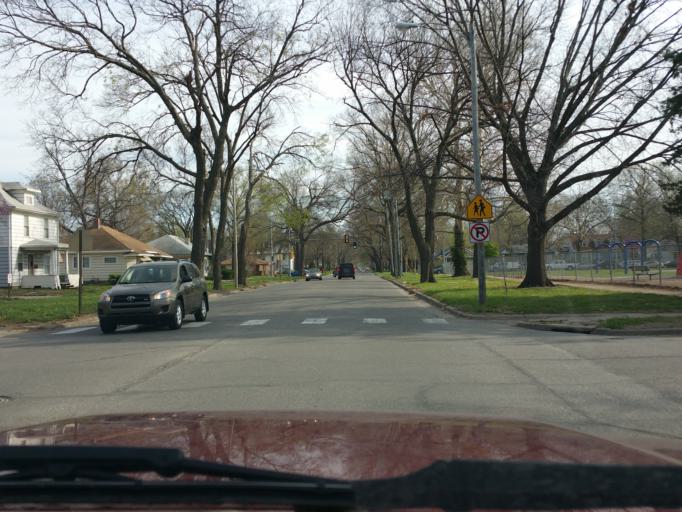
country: US
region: Kansas
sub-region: Riley County
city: Manhattan
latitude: 39.1880
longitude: -96.5666
